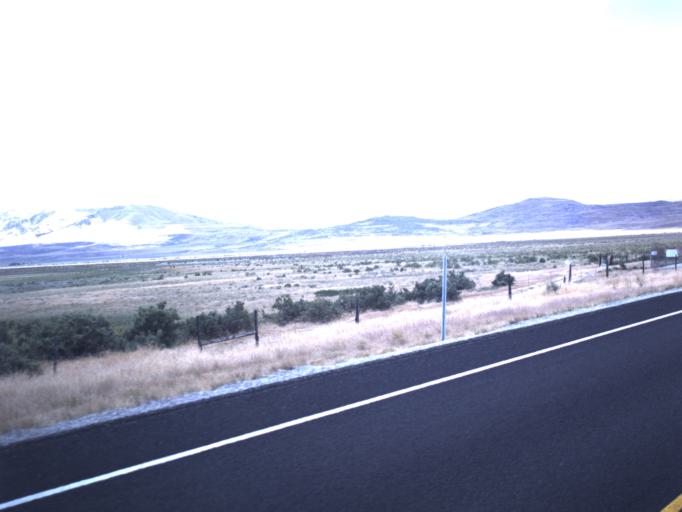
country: US
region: Utah
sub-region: Box Elder County
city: Tremonton
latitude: 41.6306
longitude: -112.4176
